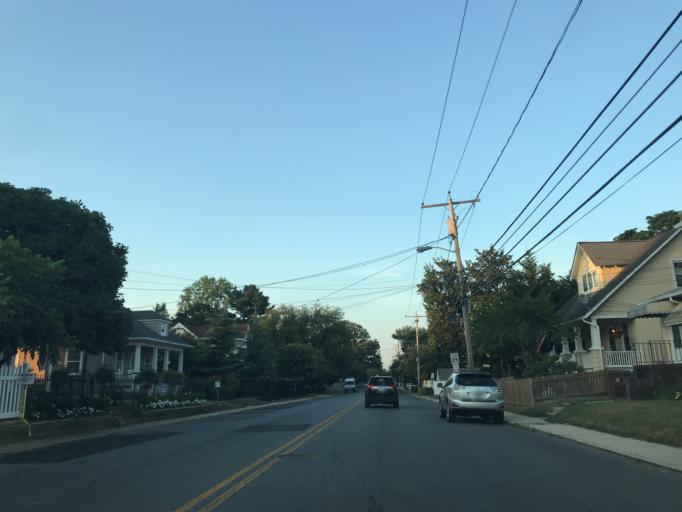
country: US
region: Maryland
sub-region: Anne Arundel County
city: Annapolis
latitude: 38.9671
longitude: -76.4867
